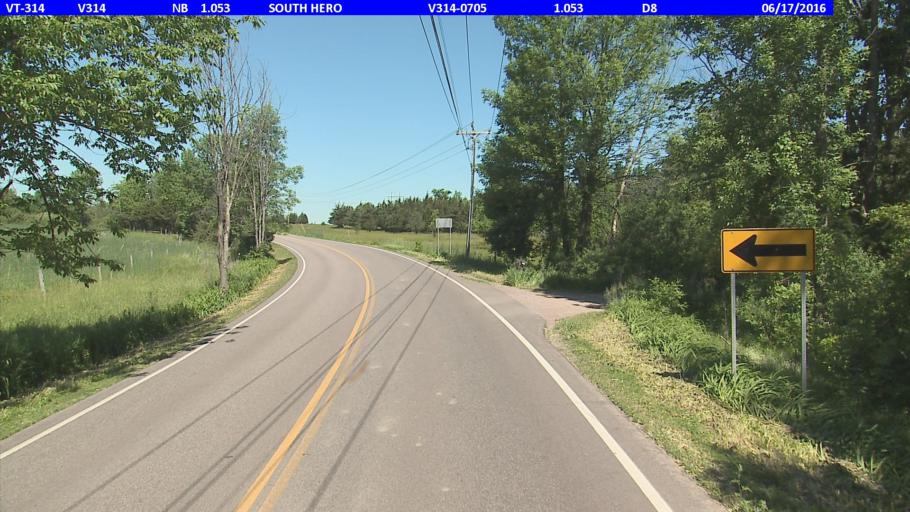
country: US
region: New York
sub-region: Clinton County
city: Cumberland Head
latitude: 44.6733
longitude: -73.3379
